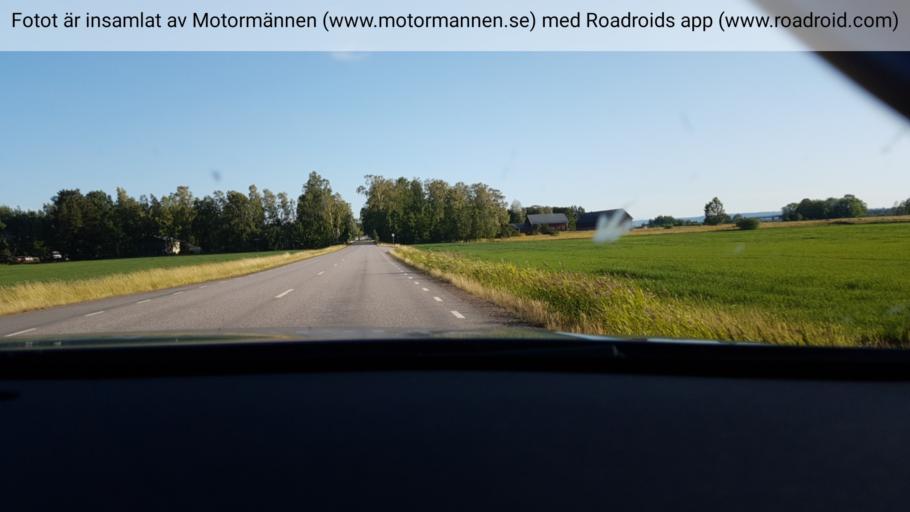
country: SE
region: Vaestra Goetaland
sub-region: Skovde Kommun
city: Stopen
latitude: 58.5575
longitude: 14.0057
